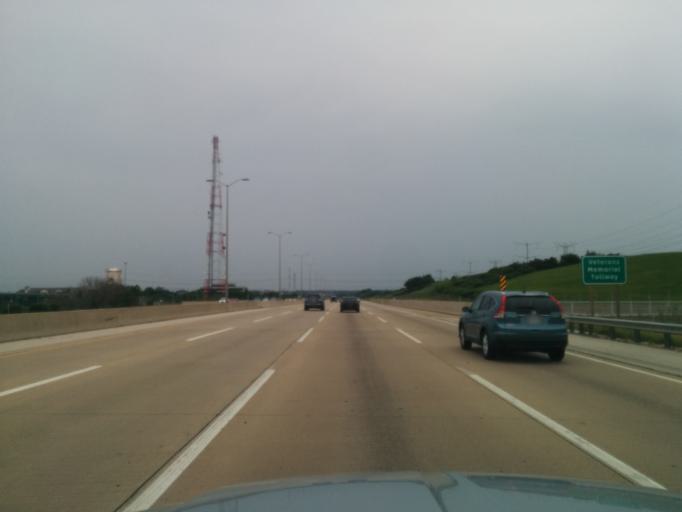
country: US
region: Illinois
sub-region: DuPage County
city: Lisle
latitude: 41.8100
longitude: -88.0480
